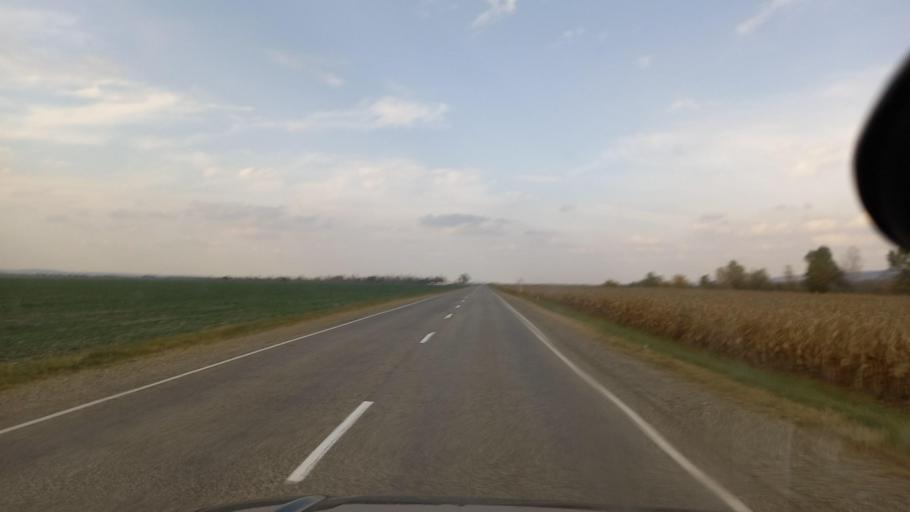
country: RU
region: Krasnodarskiy
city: Perepravnaya
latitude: 44.3394
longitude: 40.8446
